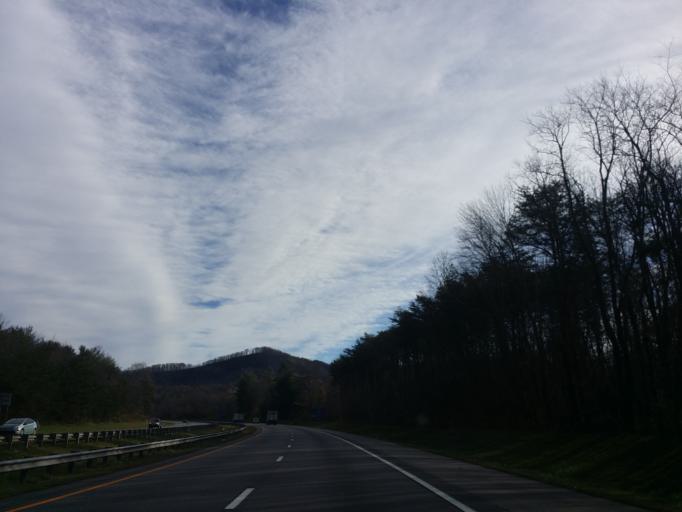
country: US
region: North Carolina
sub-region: Buncombe County
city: Black Mountain
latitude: 35.6070
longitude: -82.3300
